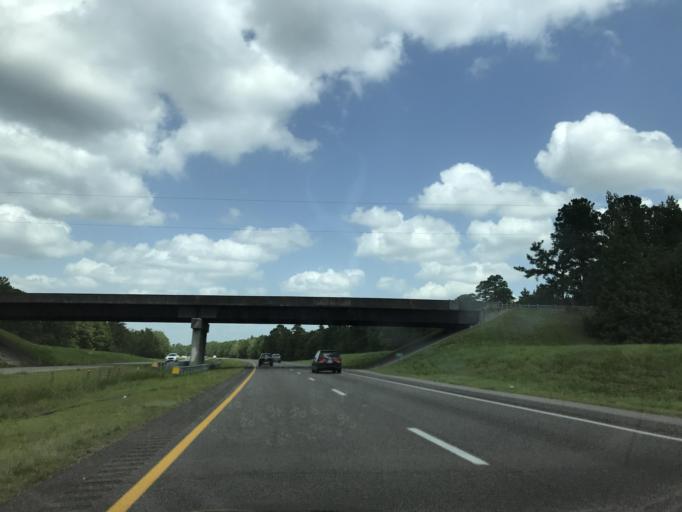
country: US
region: North Carolina
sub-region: Pender County
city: Rocky Point
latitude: 34.5030
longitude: -77.8766
